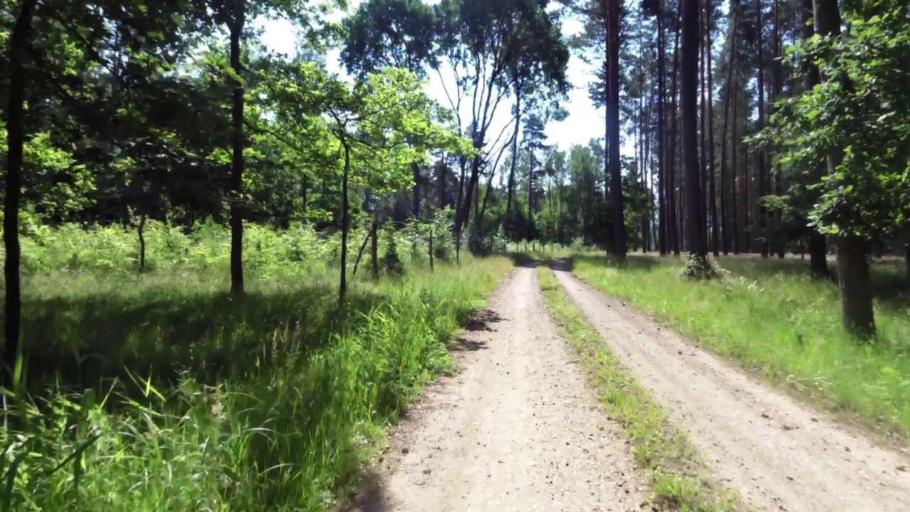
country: PL
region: West Pomeranian Voivodeship
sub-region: Powiat swidwinski
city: Polczyn-Zdroj
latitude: 53.8536
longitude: 16.1381
